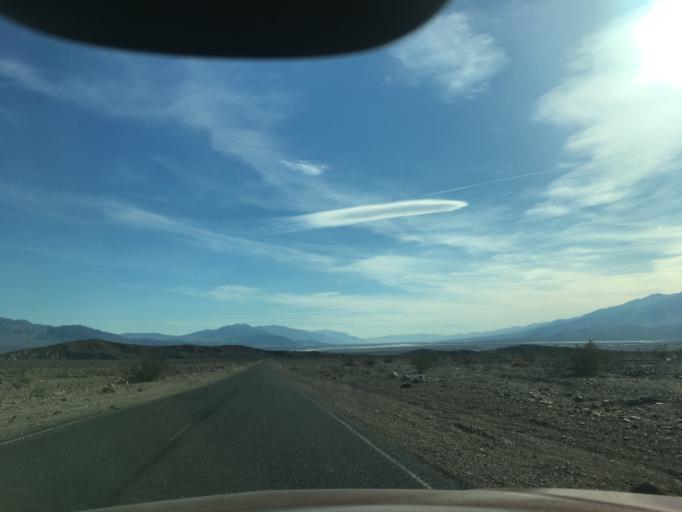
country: US
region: Nevada
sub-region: Nye County
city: Beatty
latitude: 36.6392
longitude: -116.9504
